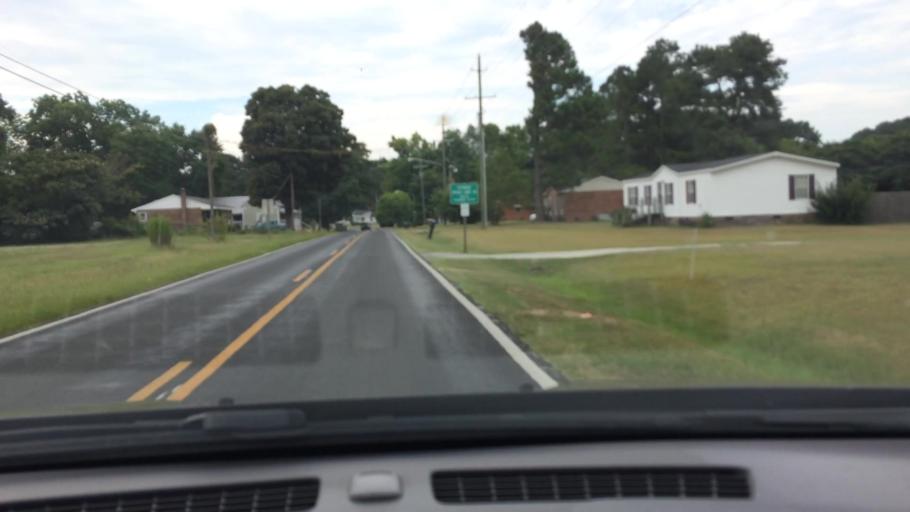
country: US
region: North Carolina
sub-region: Pitt County
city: Ayden
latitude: 35.4616
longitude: -77.4153
